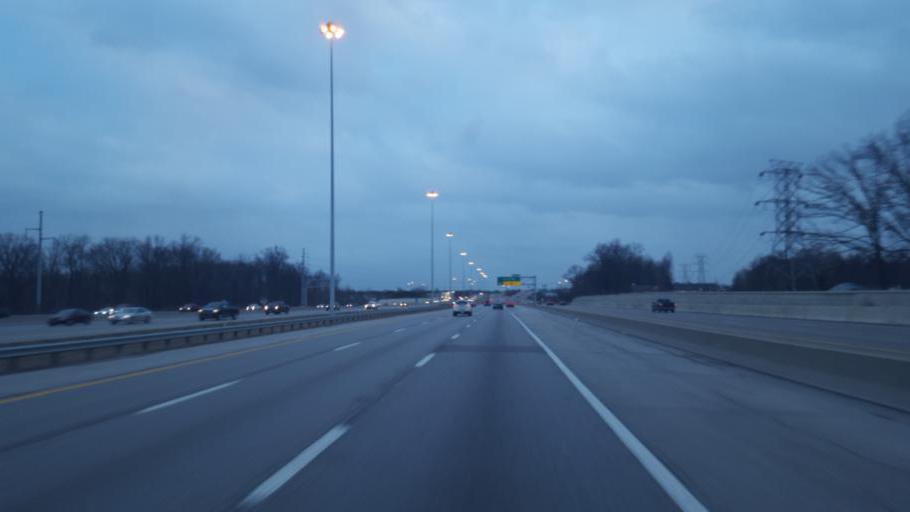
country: US
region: Ohio
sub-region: Franklin County
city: Huber Ridge
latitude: 40.0685
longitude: -82.9074
